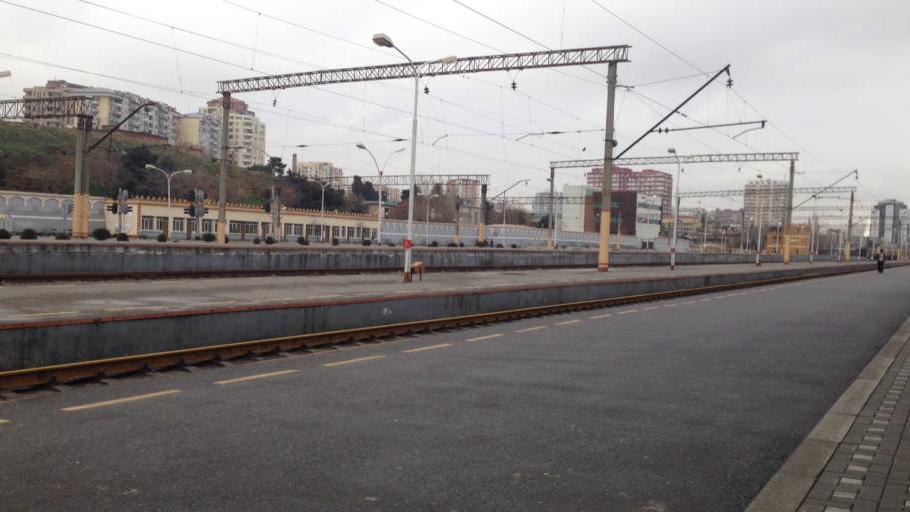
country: AZ
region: Baki
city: Baku
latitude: 40.3812
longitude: 49.8515
